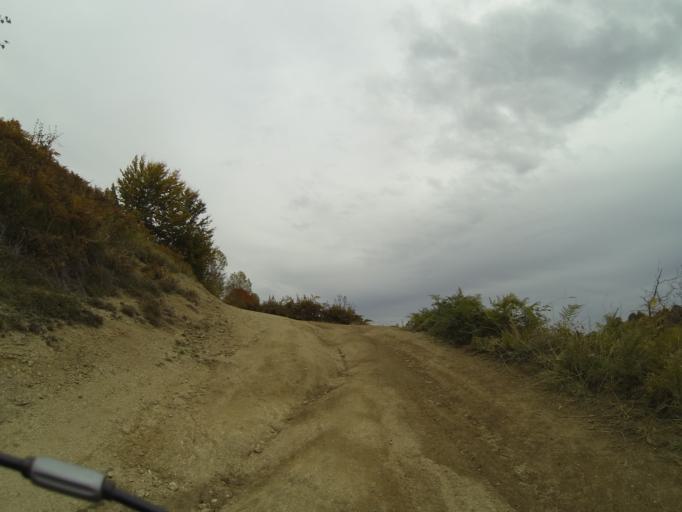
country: RO
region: Gorj
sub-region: Comuna Pades
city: Closani
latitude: 45.1054
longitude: 22.8455
